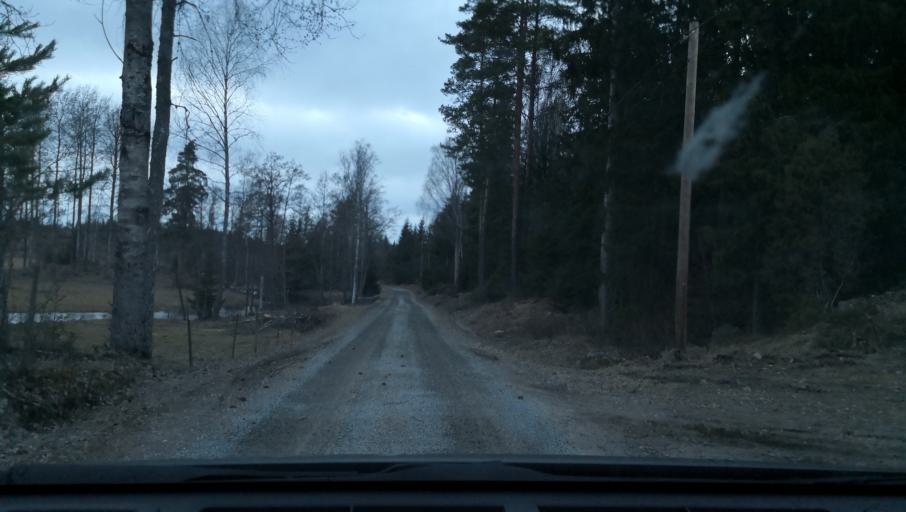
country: SE
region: OErebro
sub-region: Lindesbergs Kommun
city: Fellingsbro
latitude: 59.6087
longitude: 15.6075
